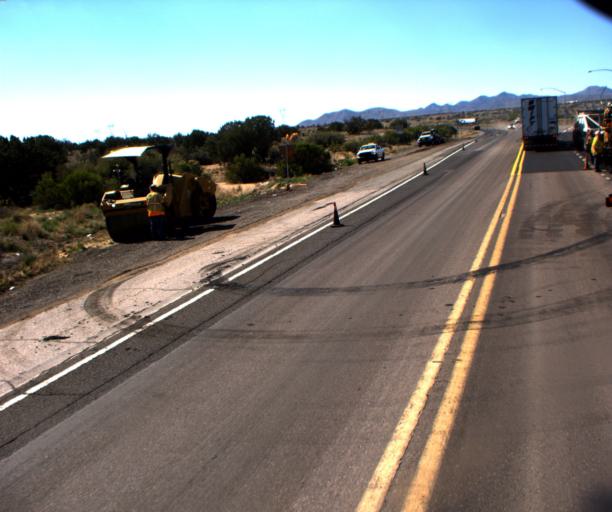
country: US
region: Arizona
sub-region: Mohave County
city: New Kingman-Butler
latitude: 35.1555
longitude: -113.6940
